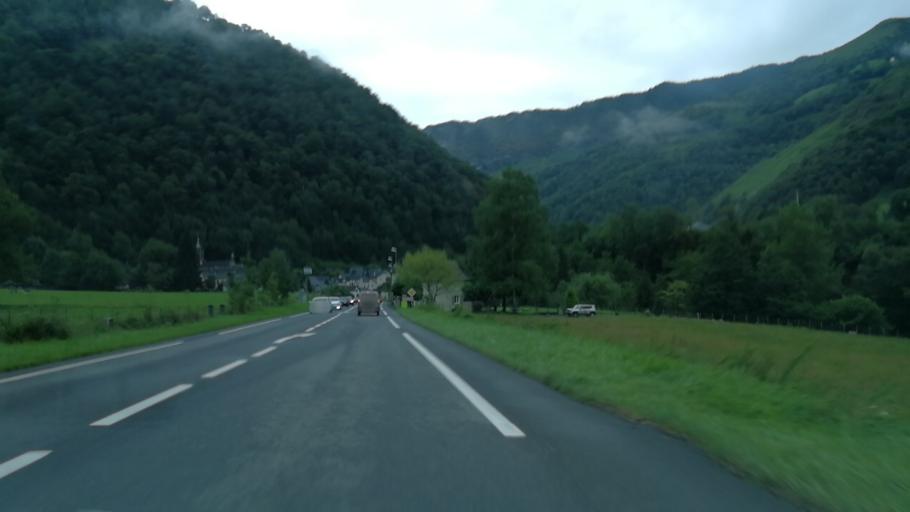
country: FR
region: Aquitaine
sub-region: Departement des Pyrenees-Atlantiques
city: Arette
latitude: 43.0479
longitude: -0.6011
